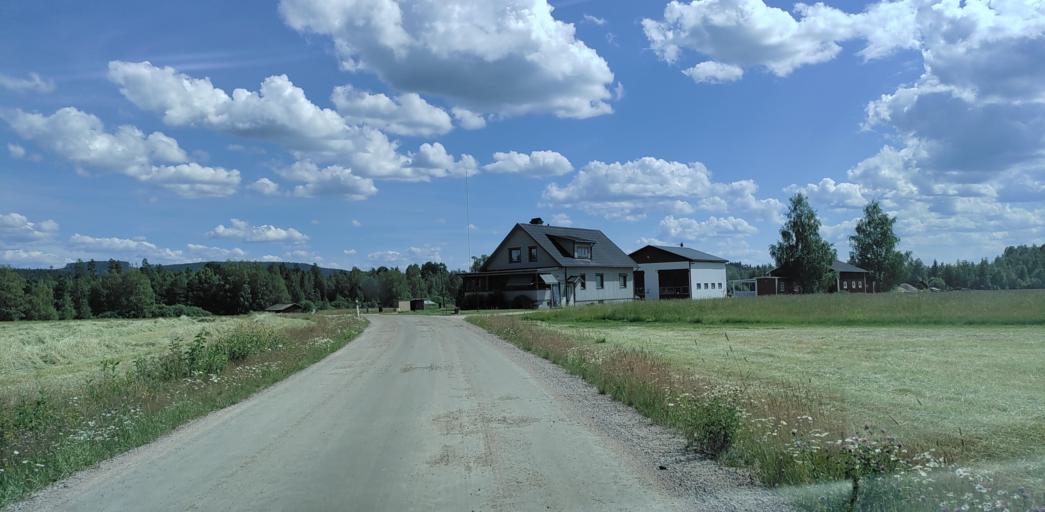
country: SE
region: Vaermland
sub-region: Hagfors Kommun
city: Ekshaerad
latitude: 60.1301
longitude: 13.4656
